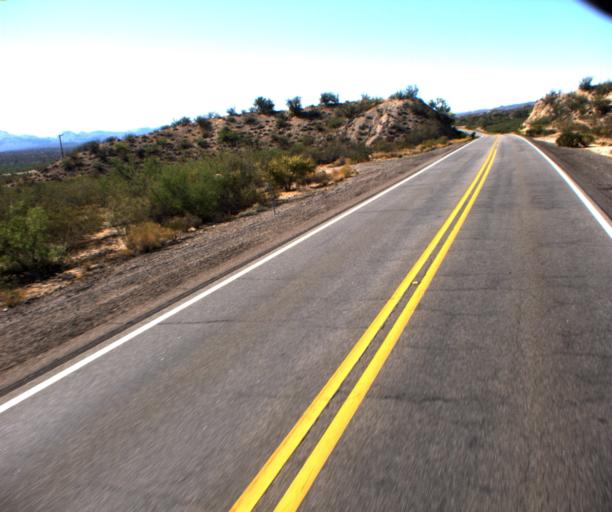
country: US
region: Arizona
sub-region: Yavapai County
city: Bagdad
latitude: 34.7781
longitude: -113.6225
